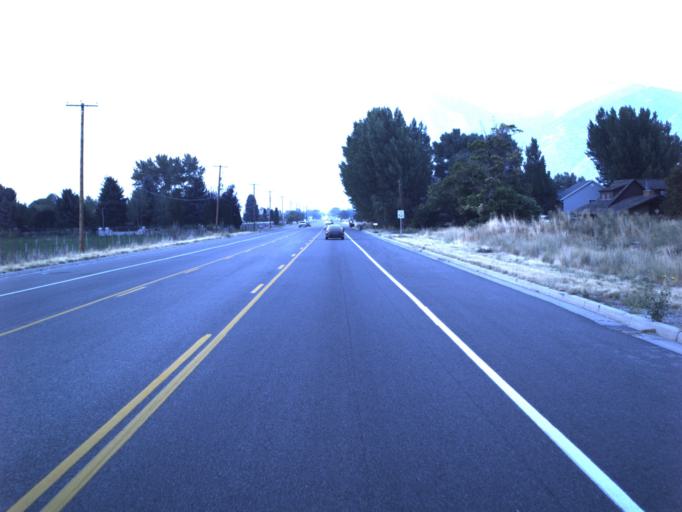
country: US
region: Utah
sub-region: Utah County
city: Mapleton
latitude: 40.1165
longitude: -111.5977
